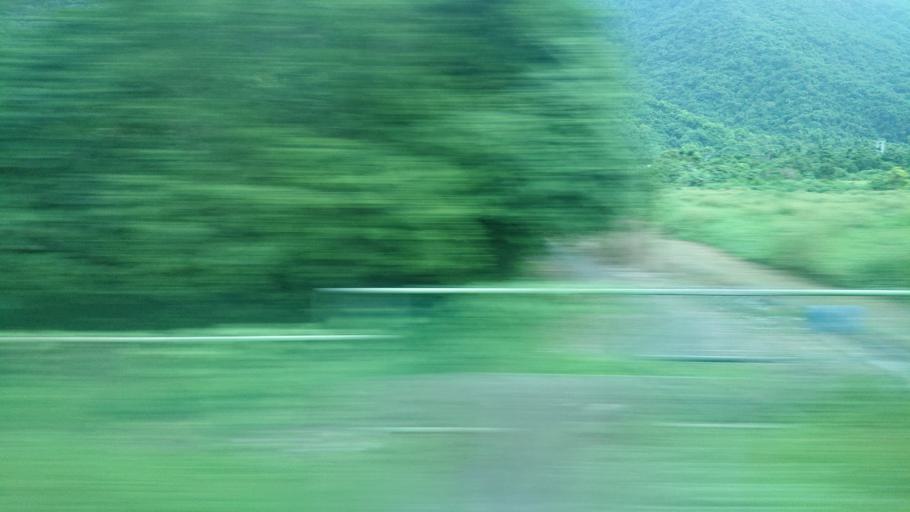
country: TW
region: Taiwan
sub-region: Hualien
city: Hualian
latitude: 24.1123
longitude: 121.6233
